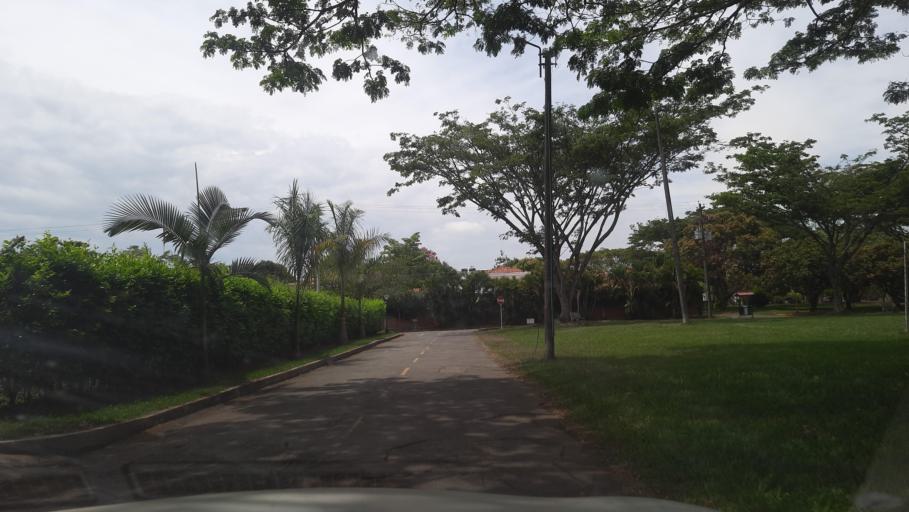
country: CO
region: Valle del Cauca
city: Jamundi
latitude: 3.2688
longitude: -76.5206
